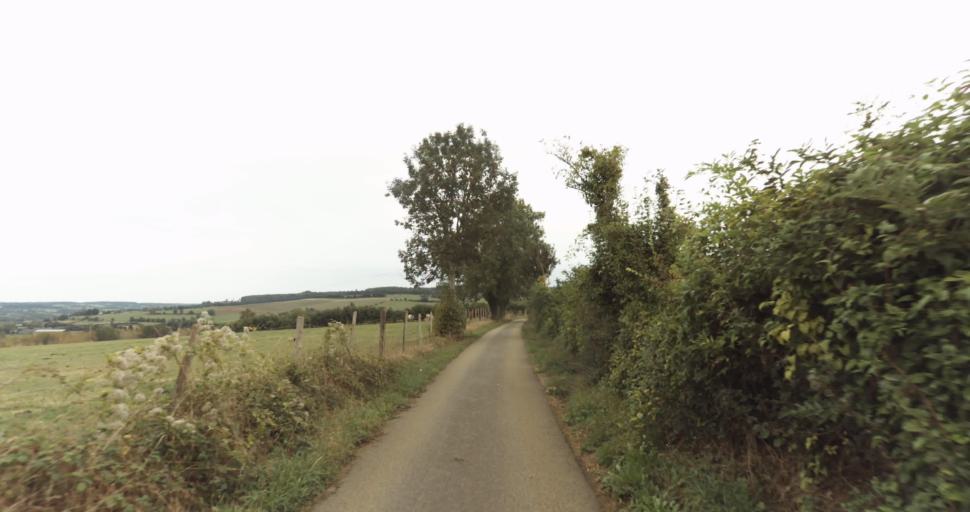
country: FR
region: Lower Normandy
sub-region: Departement de l'Orne
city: Gace
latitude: 48.7615
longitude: 0.3229
